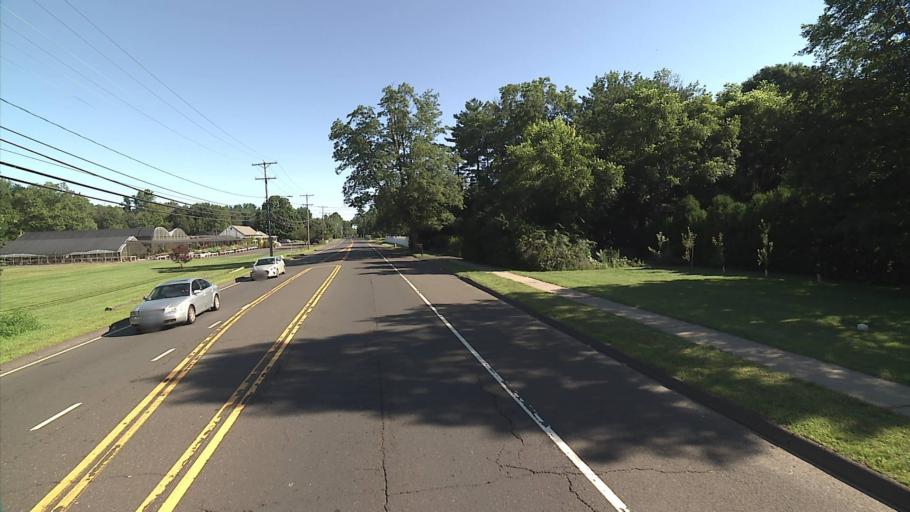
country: US
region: Connecticut
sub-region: New Haven County
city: Cheshire
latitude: 41.4677
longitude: -72.9068
